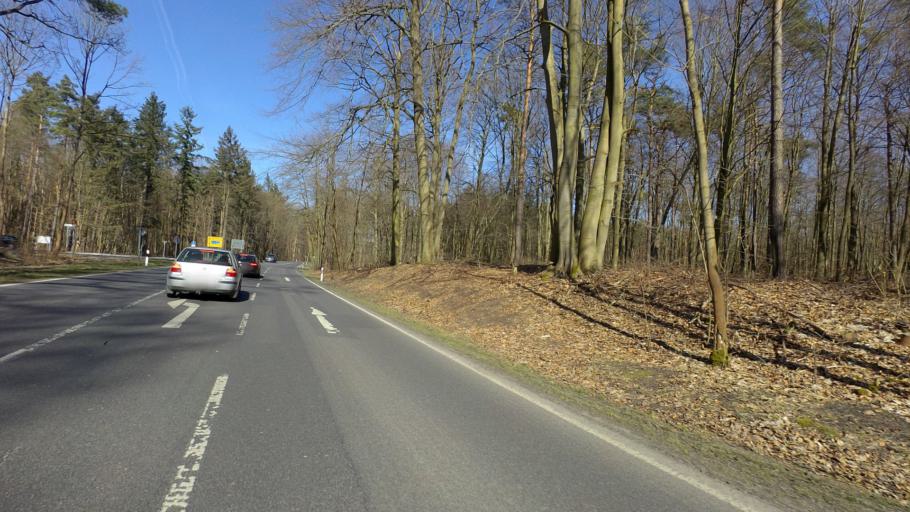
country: DE
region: Brandenburg
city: Eberswalde
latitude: 52.8615
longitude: 13.8336
